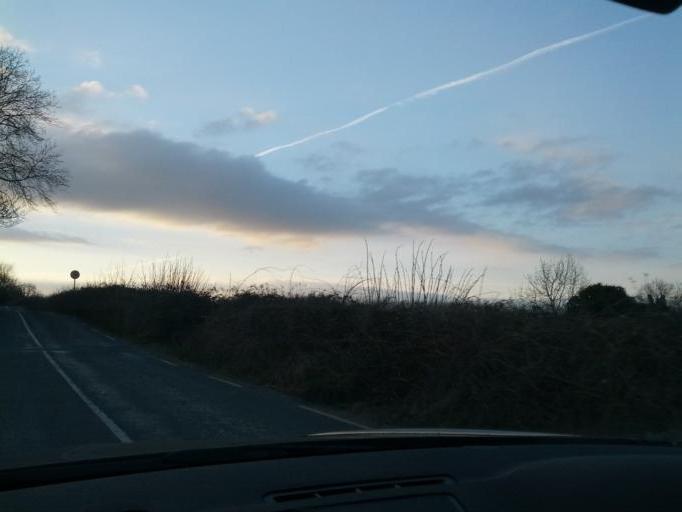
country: IE
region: Munster
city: Nenagh Bridge
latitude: 52.9288
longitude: -8.2337
